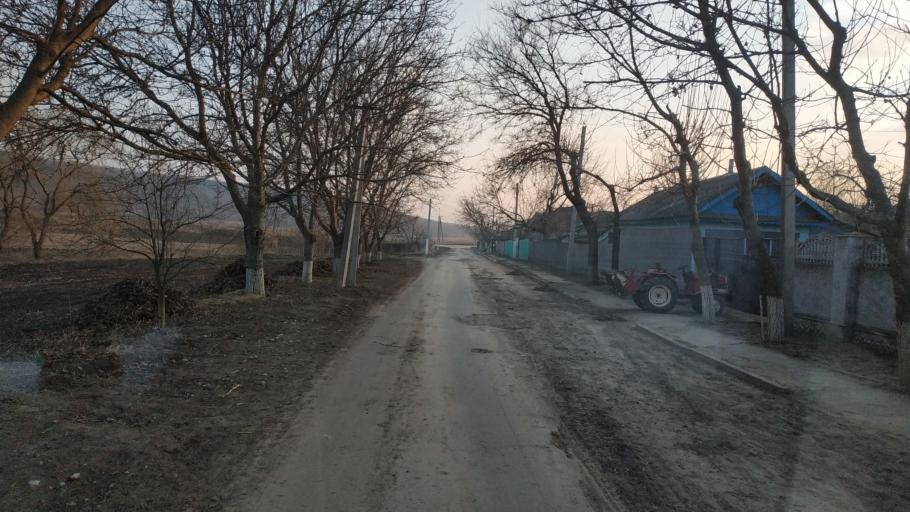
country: MD
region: Hincesti
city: Dancu
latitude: 46.7063
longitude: 28.3450
